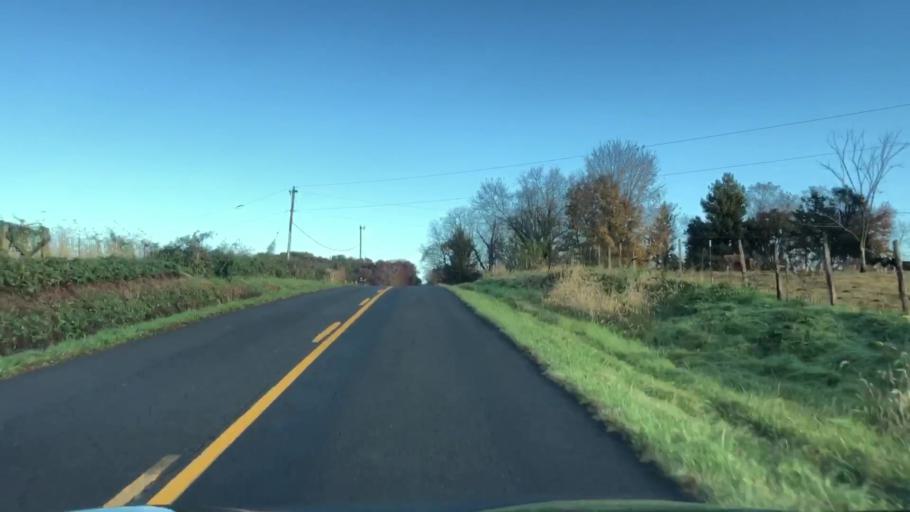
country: US
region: Virginia
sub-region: Prince William County
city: Nokesville
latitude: 38.6828
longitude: -77.6673
